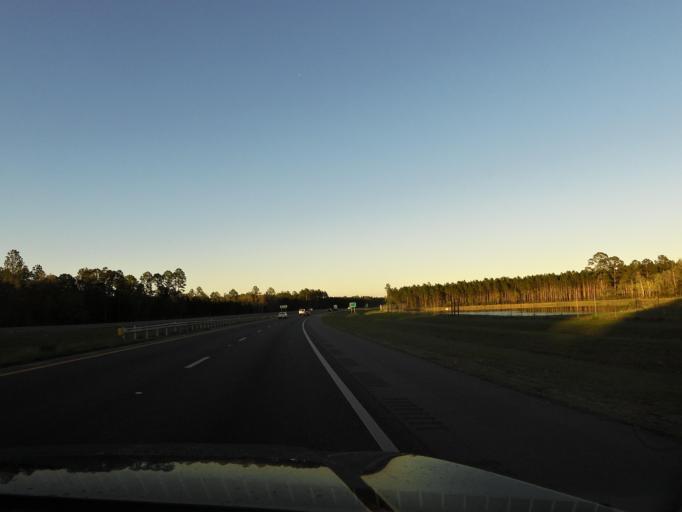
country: US
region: Florida
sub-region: Bradford County
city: Starke
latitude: 29.9824
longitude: -82.1146
